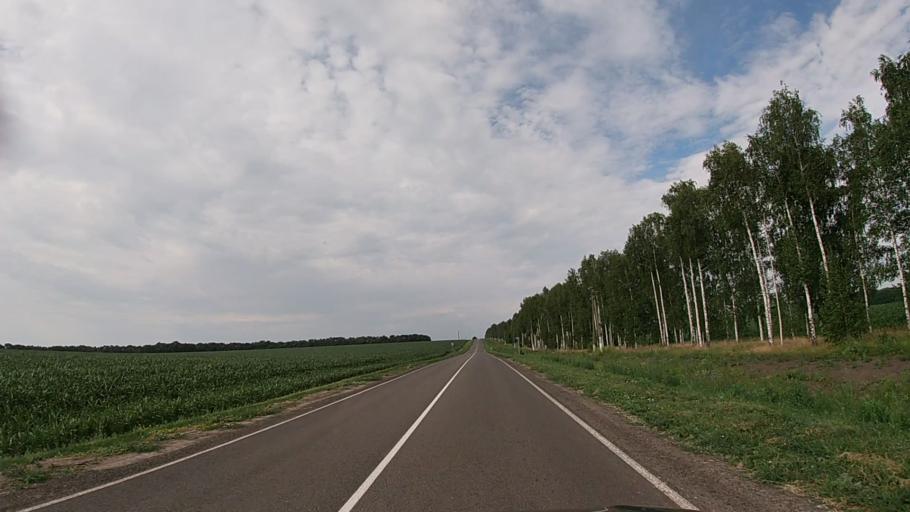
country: RU
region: Belgorod
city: Krasnaya Yaruga
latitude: 50.8237
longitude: 35.4643
